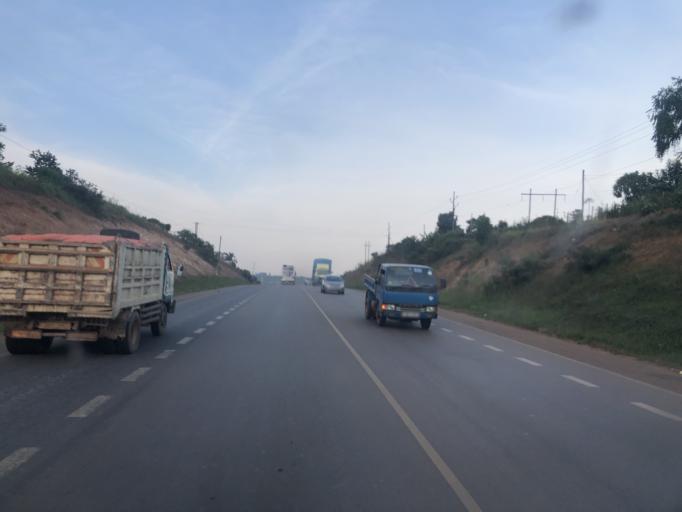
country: UG
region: Central Region
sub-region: Mpigi District
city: Mpigi
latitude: 0.2439
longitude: 32.3769
